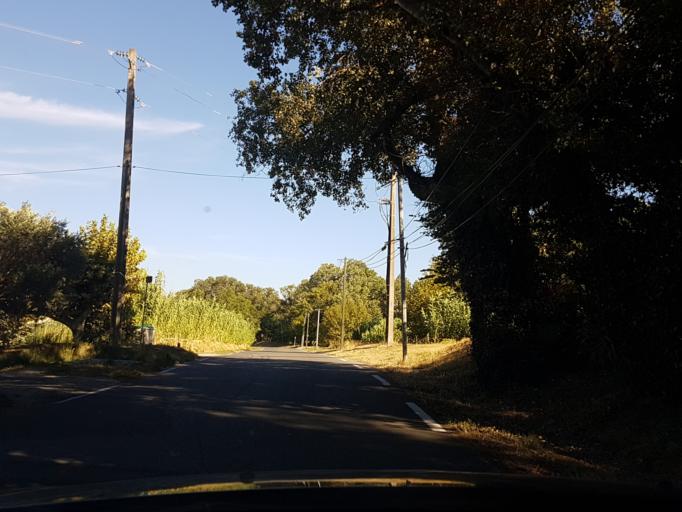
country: FR
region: Provence-Alpes-Cote d'Azur
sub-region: Departement du Vaucluse
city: Monteux
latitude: 44.0398
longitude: 4.9791
